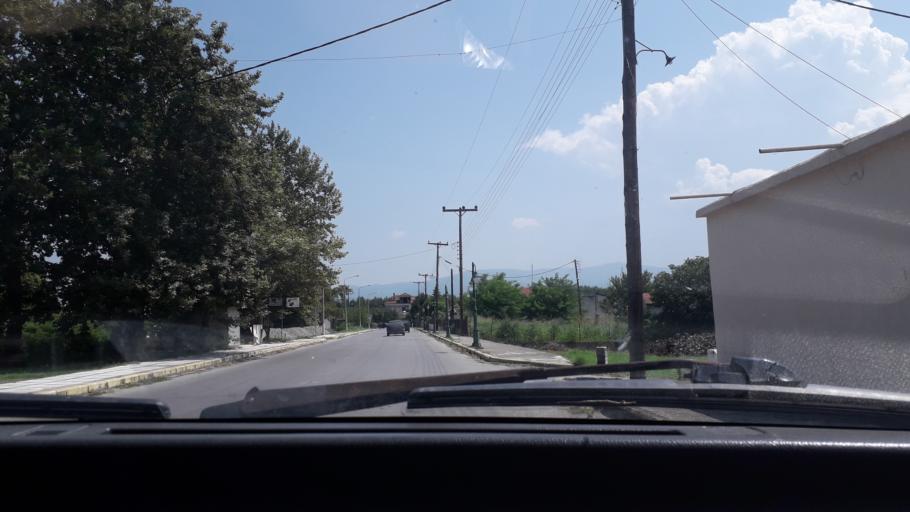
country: GR
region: Central Macedonia
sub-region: Nomos Pellis
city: Tsakoi
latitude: 40.9554
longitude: 22.0421
